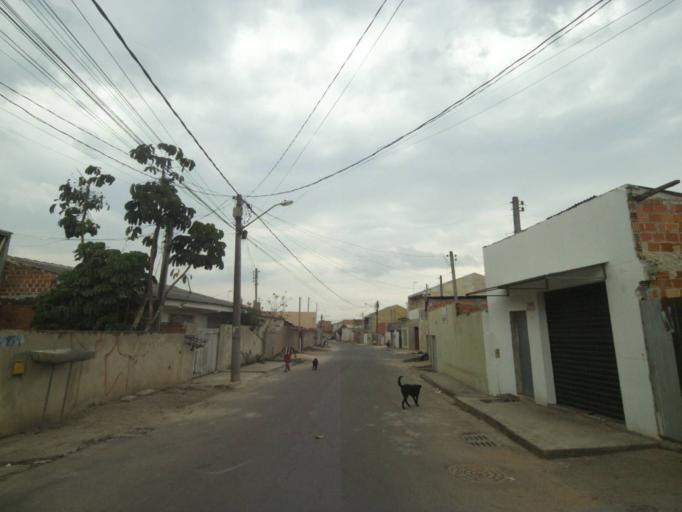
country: BR
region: Parana
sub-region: Sao Jose Dos Pinhais
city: Sao Jose dos Pinhais
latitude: -25.4942
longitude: -49.2003
